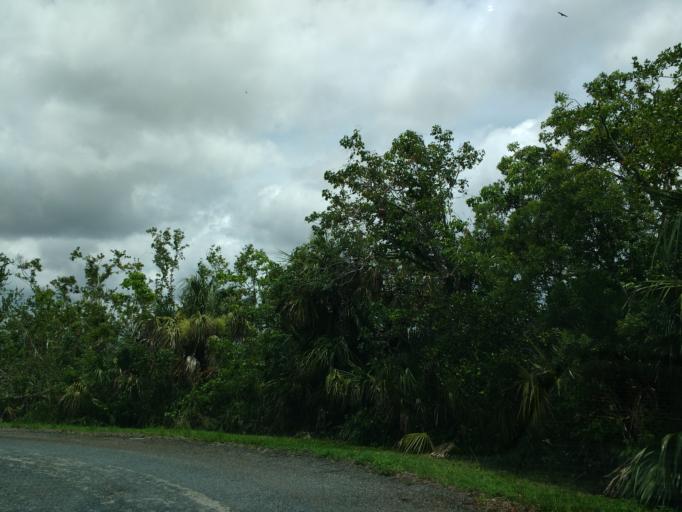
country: US
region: Florida
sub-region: Miami-Dade County
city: Florida City
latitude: 25.2818
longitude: -80.7995
